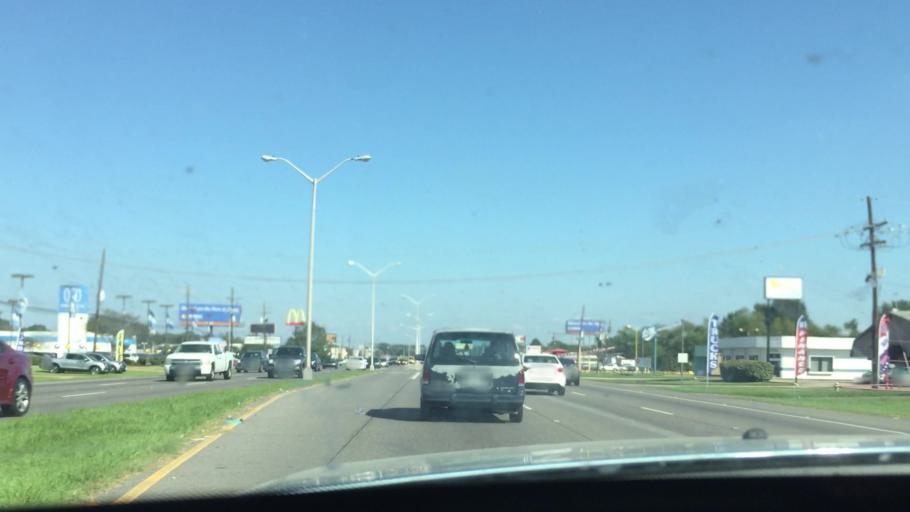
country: US
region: Louisiana
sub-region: East Baton Rouge Parish
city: Westminster
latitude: 30.4518
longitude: -91.1083
